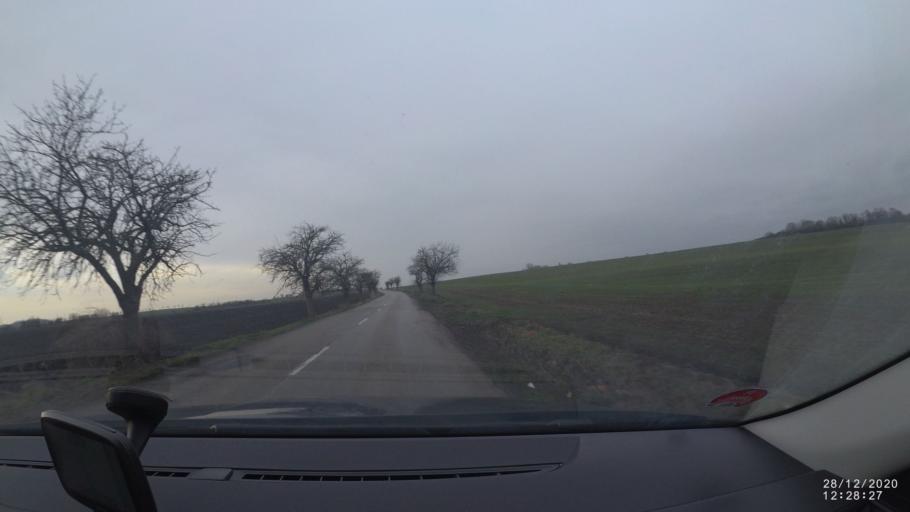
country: CZ
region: Central Bohemia
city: Brandys nad Labem-Stara Boleslav
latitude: 50.1953
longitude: 14.6308
